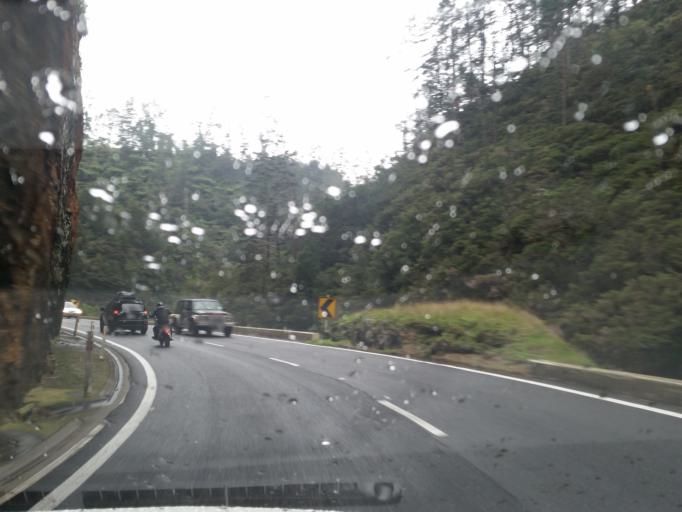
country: NZ
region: Waikato
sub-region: Hauraki District
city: Paeroa
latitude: -37.4226
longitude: 175.7302
